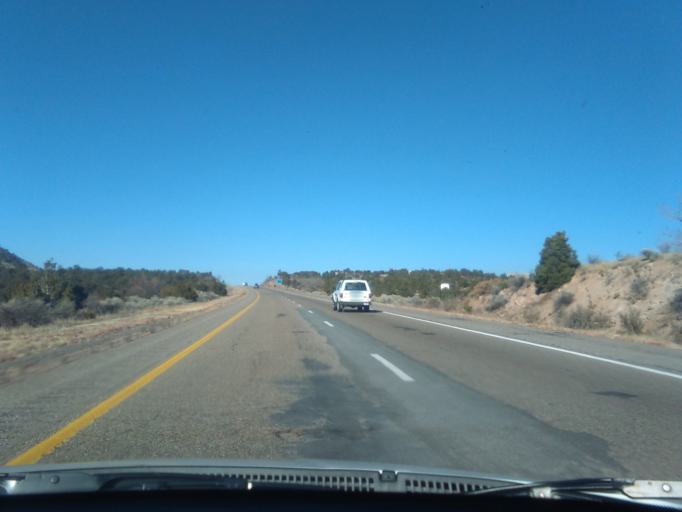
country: US
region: New Mexico
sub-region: Santa Fe County
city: Eldorado at Santa Fe
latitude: 35.5420
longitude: -105.8643
